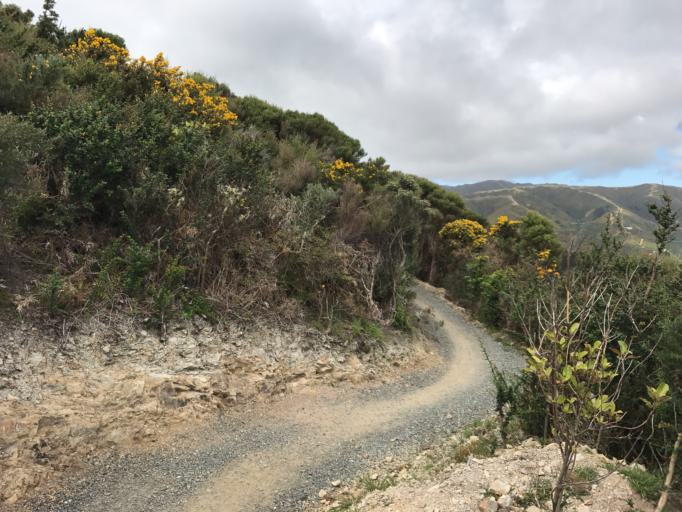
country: NZ
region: Wellington
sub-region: Wellington City
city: Brooklyn
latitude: -41.2931
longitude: 174.7076
